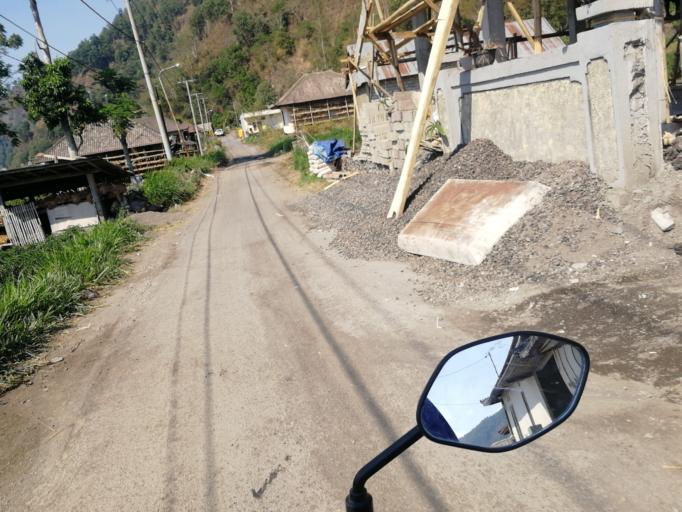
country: ID
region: Bali
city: Banjar Trunyan
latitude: -8.2649
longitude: 115.4204
